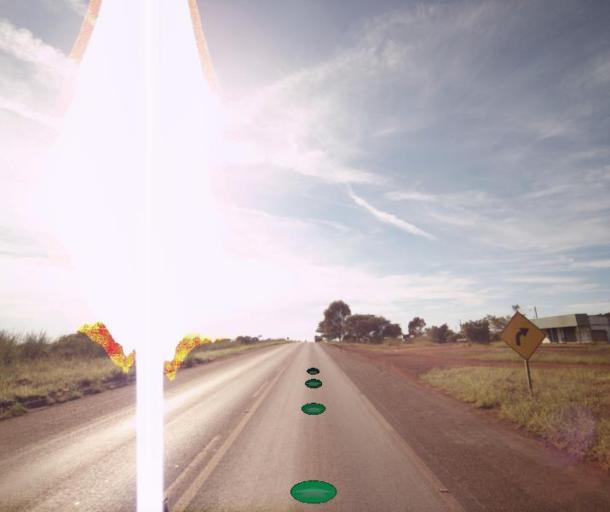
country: BR
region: Federal District
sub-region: Brasilia
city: Brasilia
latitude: -15.7379
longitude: -48.3918
